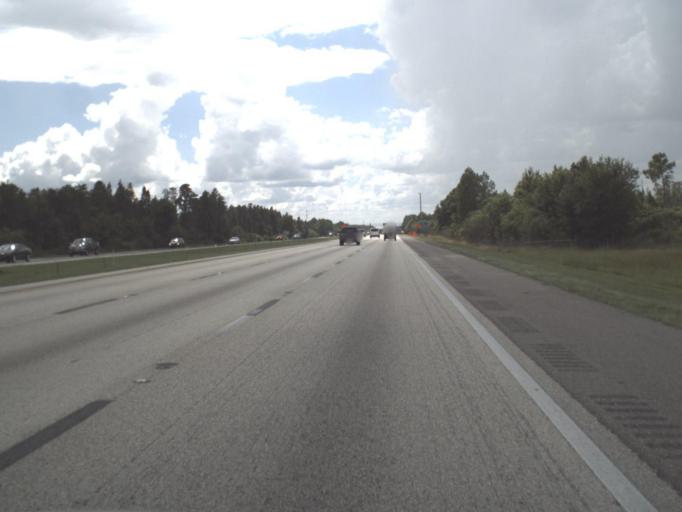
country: US
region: Florida
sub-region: Polk County
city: Lake Alfred
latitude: 28.1892
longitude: -81.7264
